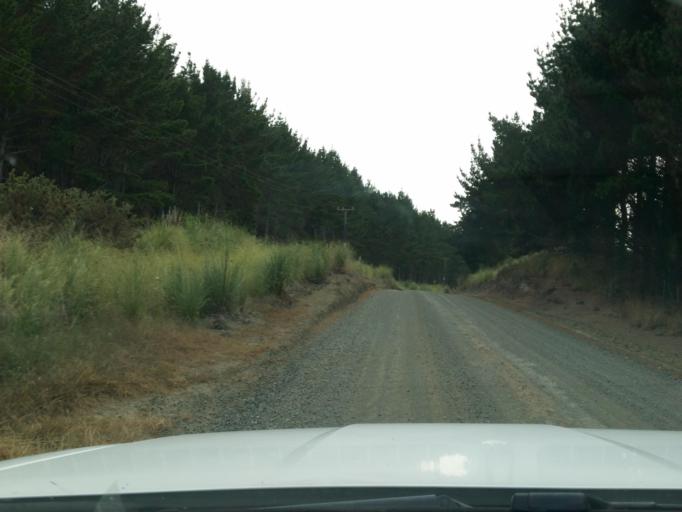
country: NZ
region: Northland
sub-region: Kaipara District
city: Dargaville
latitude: -36.2384
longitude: 174.0507
